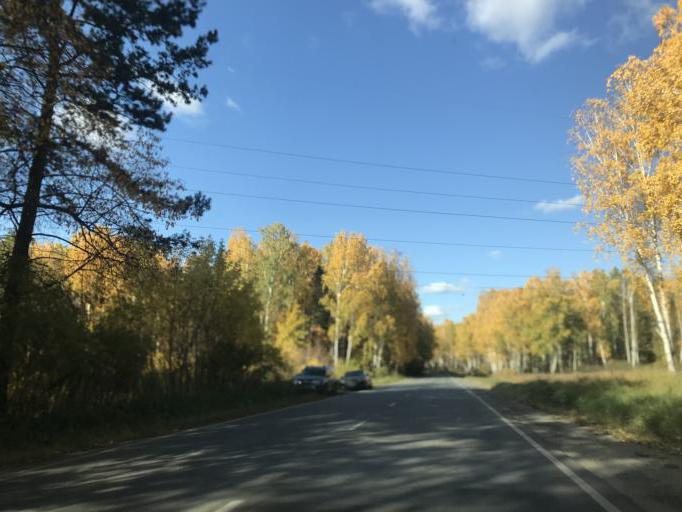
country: RU
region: Chelyabinsk
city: Dolgoderevenskoye
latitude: 55.2688
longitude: 61.3649
